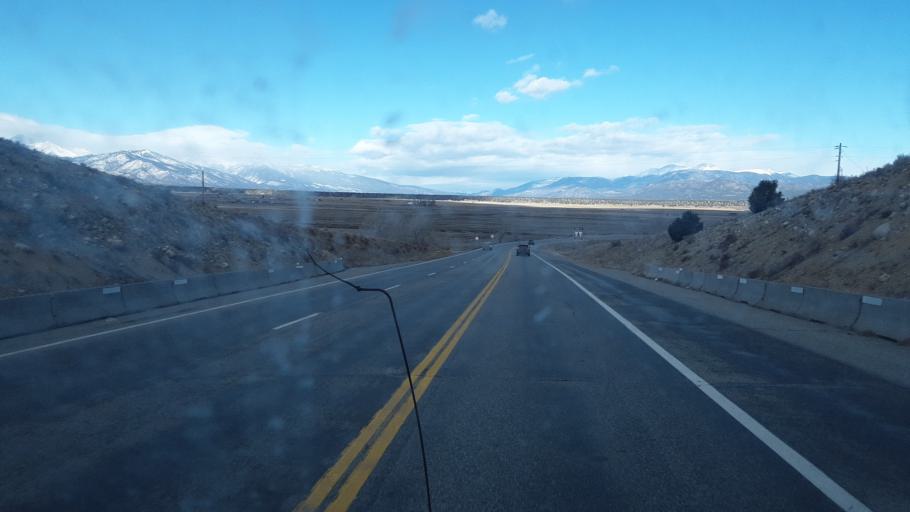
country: US
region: Colorado
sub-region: Chaffee County
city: Buena Vista
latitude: 38.7067
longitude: -106.0906
